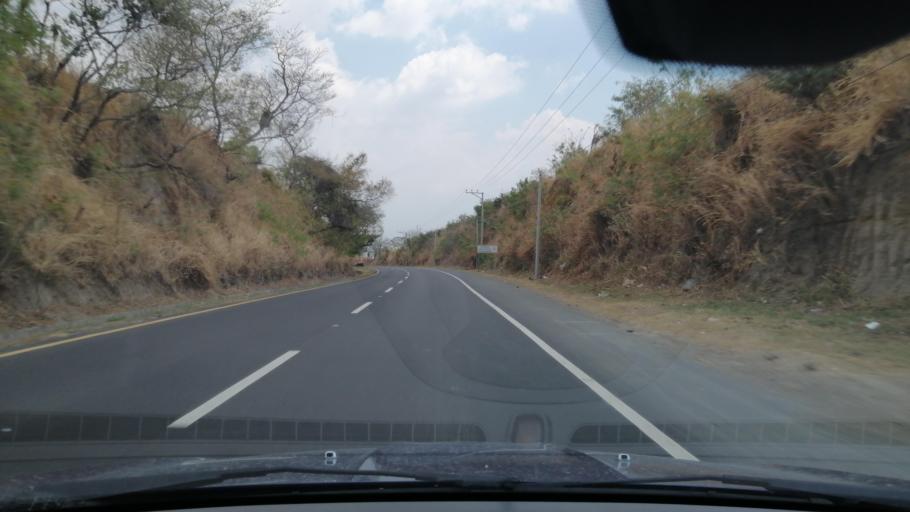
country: SV
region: La Libertad
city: Ciudad Arce
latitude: 13.8600
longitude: -89.4824
